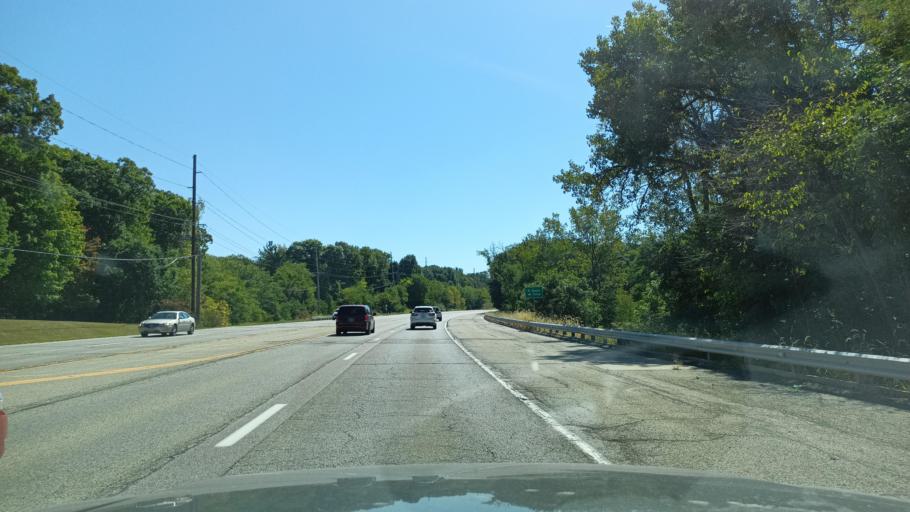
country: US
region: Illinois
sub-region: Peoria County
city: Peoria Heights
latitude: 40.7660
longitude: -89.6431
